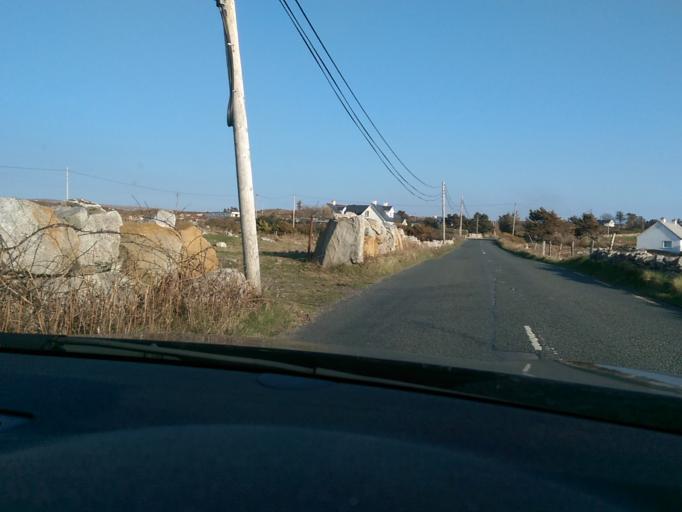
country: IE
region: Connaught
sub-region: County Galway
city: Clifden
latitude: 53.3195
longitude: -9.8086
